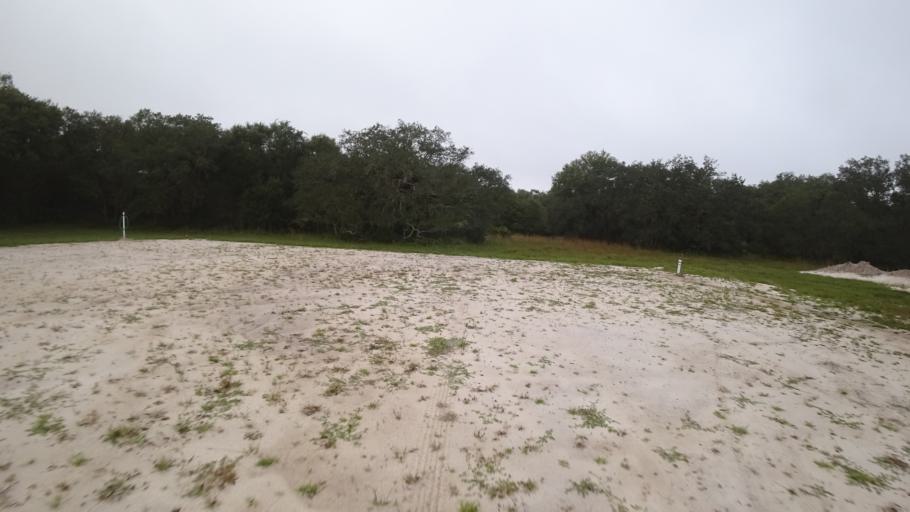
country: US
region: Florida
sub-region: Sarasota County
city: Lake Sarasota
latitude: 27.2931
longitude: -82.2224
